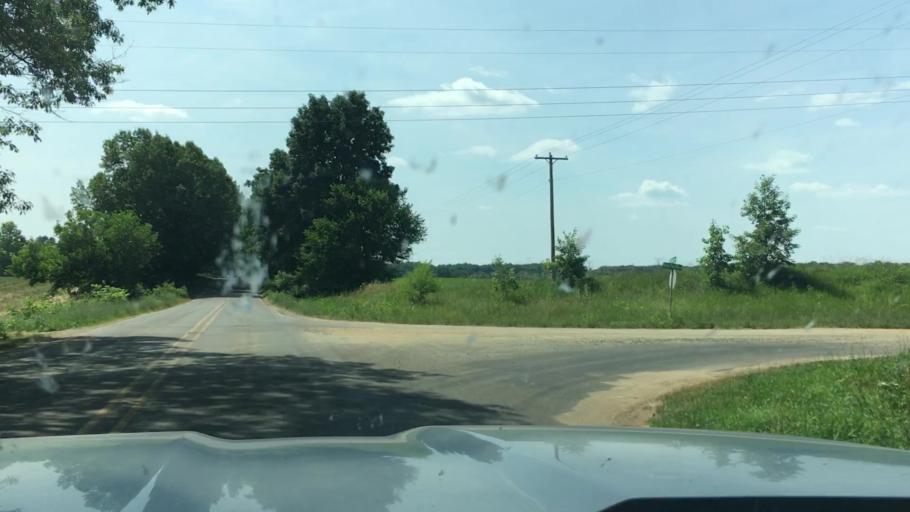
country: US
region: Michigan
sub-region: Barry County
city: Stony Point
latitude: 42.4286
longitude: -85.5037
